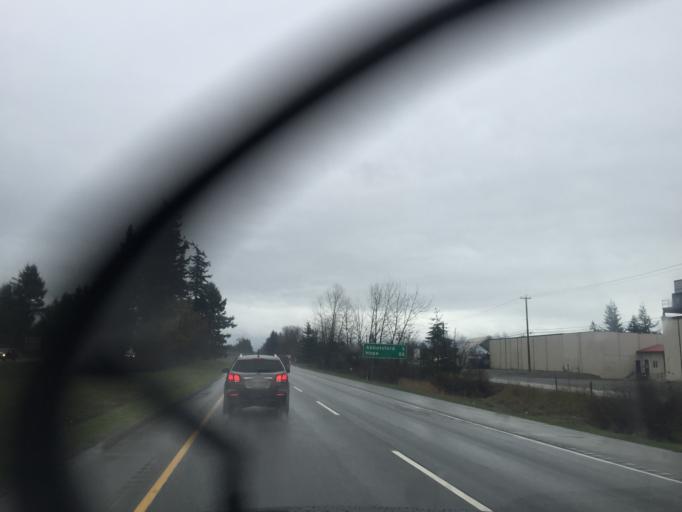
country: CA
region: British Columbia
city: Aldergrove
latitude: 49.0496
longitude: -122.3627
